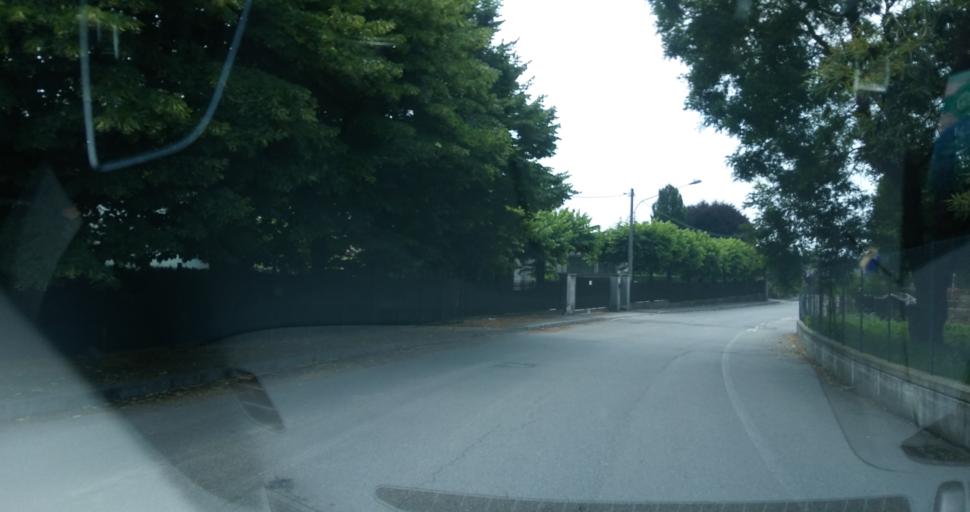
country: IT
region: Lombardy
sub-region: Provincia di Varese
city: Bardello
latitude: 45.8422
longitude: 8.6945
